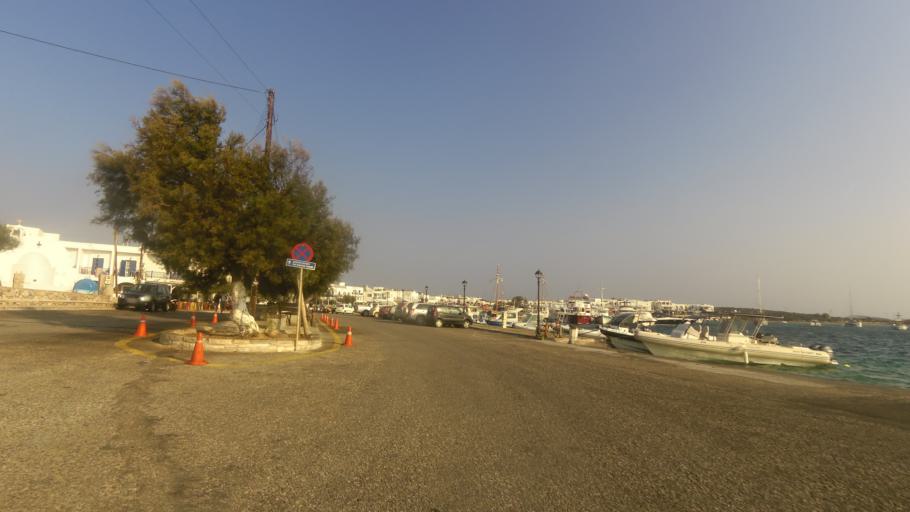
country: GR
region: South Aegean
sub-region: Nomos Kykladon
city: Antiparos
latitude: 37.0395
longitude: 25.0852
